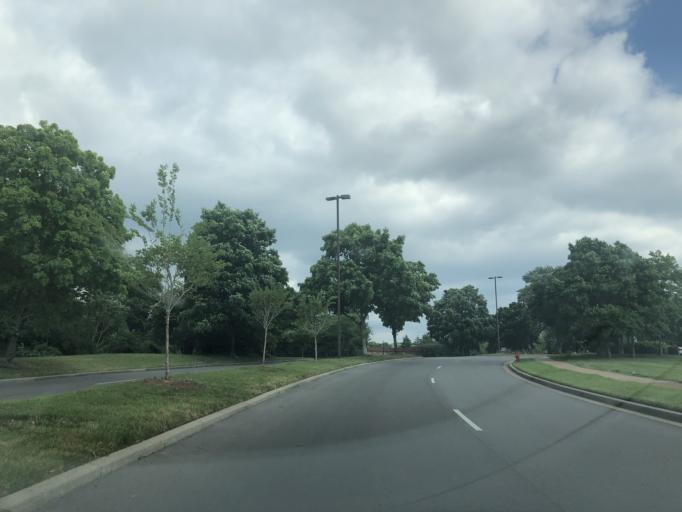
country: US
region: Tennessee
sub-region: Davidson County
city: Belle Meade
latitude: 36.0962
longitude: -86.8206
